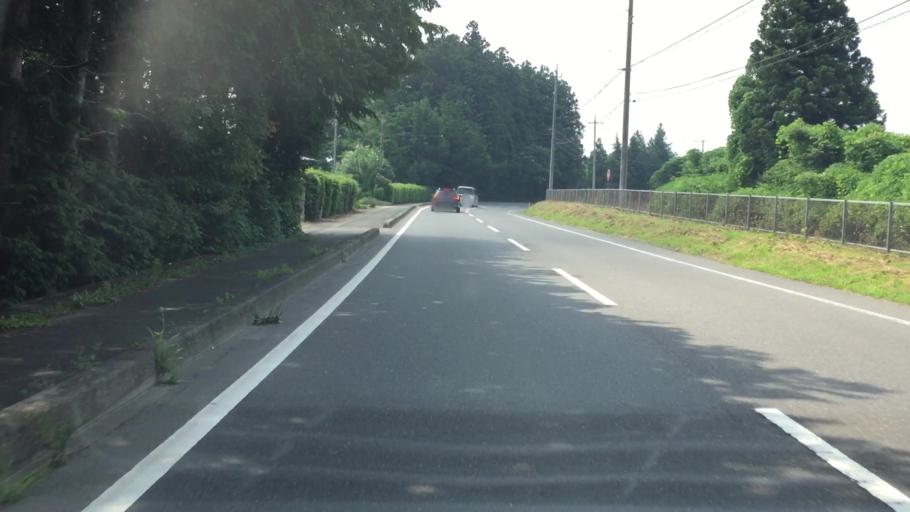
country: JP
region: Tochigi
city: Kuroiso
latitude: 37.0058
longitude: 139.9995
